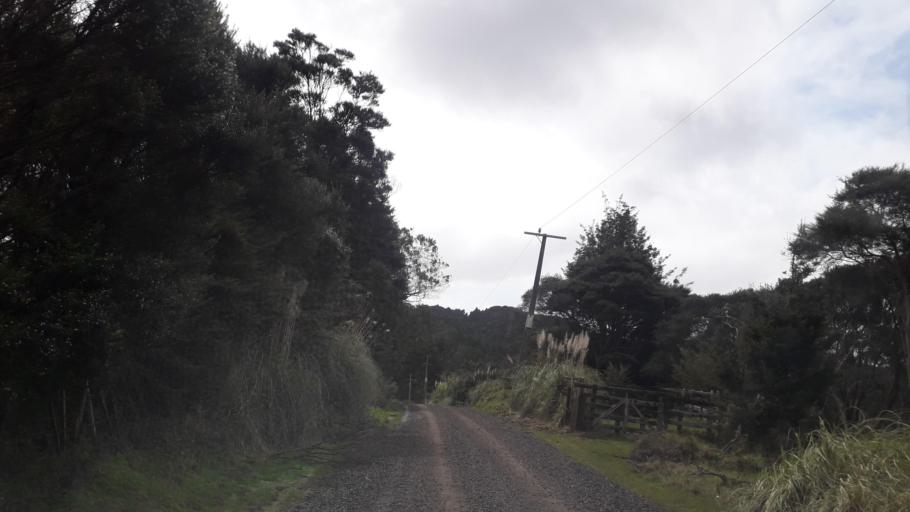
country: NZ
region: Northland
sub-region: Far North District
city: Kaitaia
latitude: -35.3852
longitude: 173.4063
